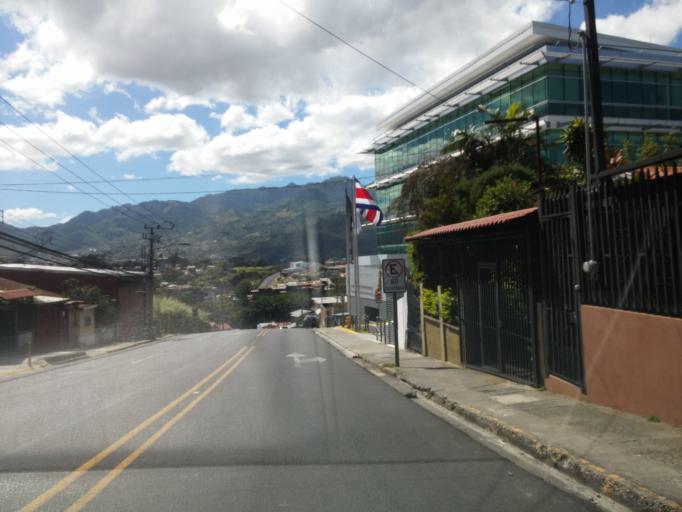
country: CR
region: San Jose
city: San Jose
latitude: 9.9287
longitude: -84.1039
